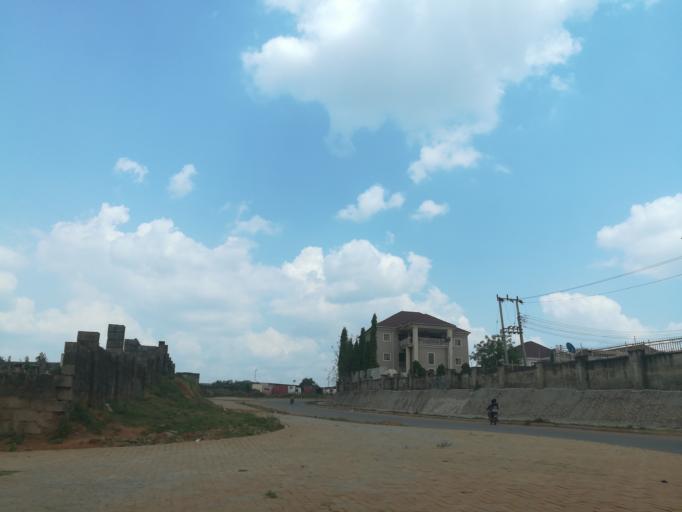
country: NG
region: Abuja Federal Capital Territory
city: Abuja
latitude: 9.0580
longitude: 7.4466
